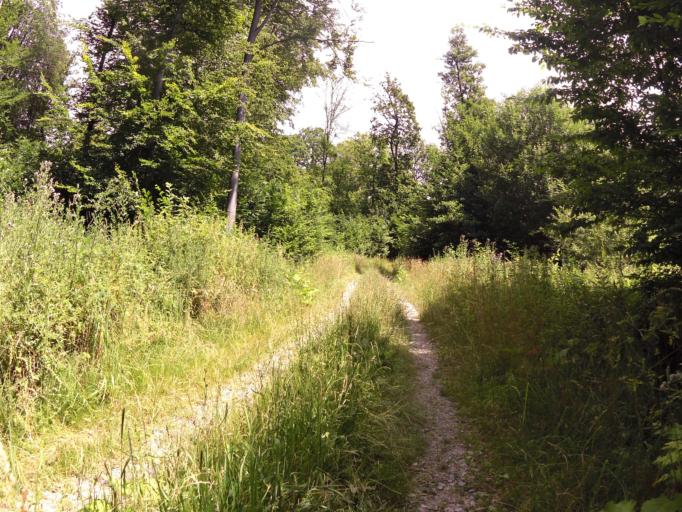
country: DE
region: Bavaria
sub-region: Regierungsbezirk Unterfranken
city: Kleinrinderfeld
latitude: 49.7076
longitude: 9.8749
